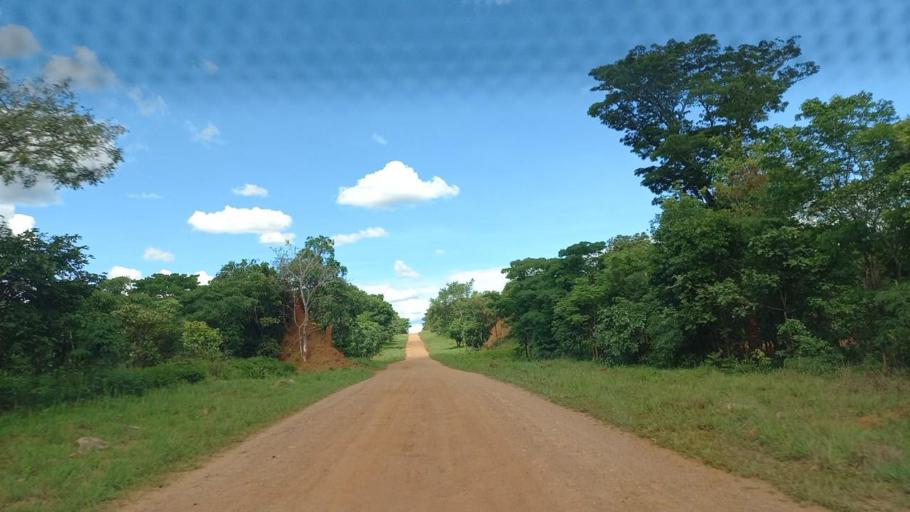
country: ZM
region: North-Western
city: Mwinilunga
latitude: -12.1142
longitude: 24.2823
